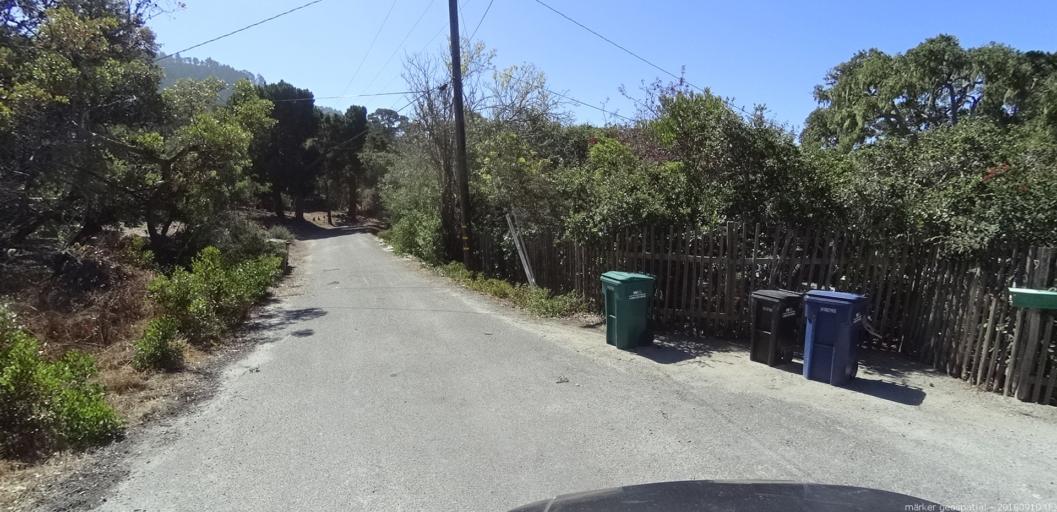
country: US
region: California
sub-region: Monterey County
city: Carmel-by-the-Sea
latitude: 36.5068
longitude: -121.9342
